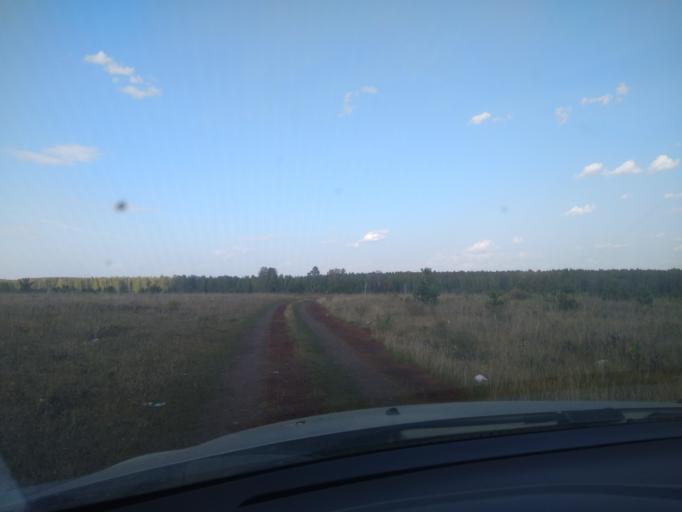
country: RU
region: Sverdlovsk
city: Pokrovskoye
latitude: 56.4242
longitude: 61.6089
